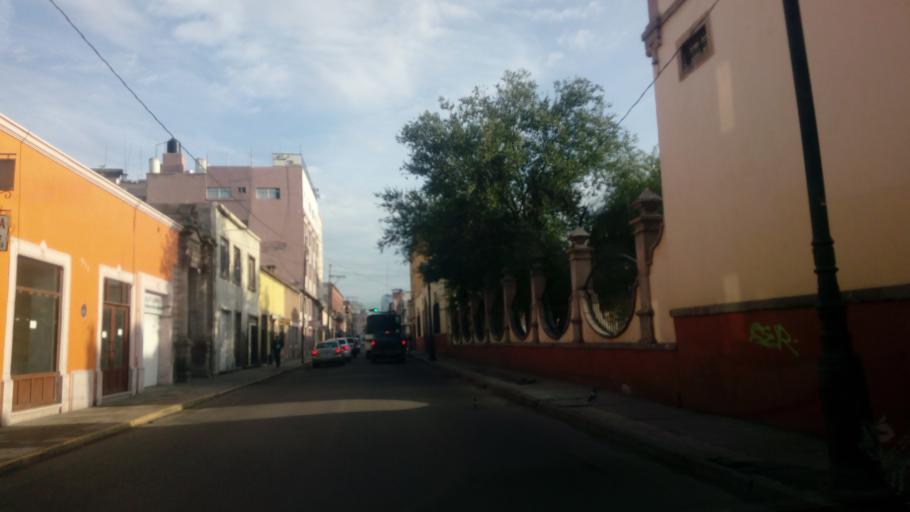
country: MX
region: Durango
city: Victoria de Durango
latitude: 24.0214
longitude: -104.6696
